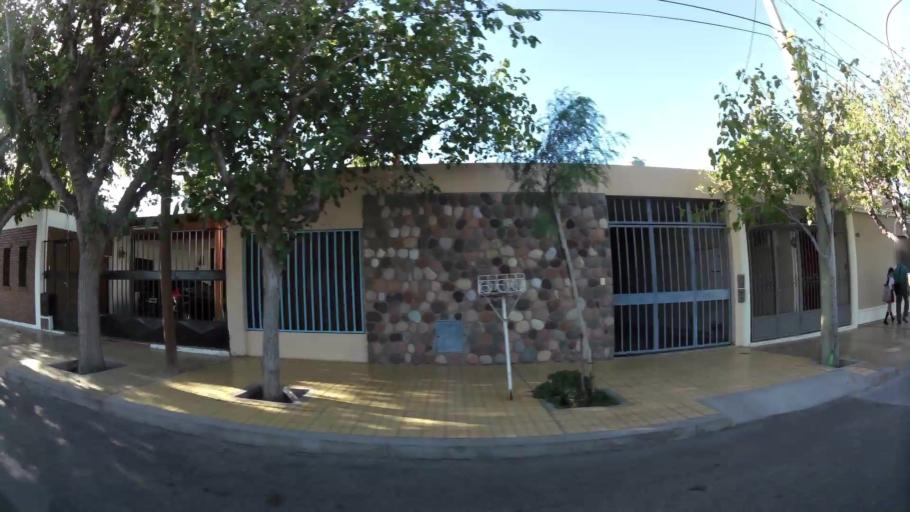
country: AR
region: San Juan
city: Villa Krause
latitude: -31.5508
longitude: -68.5187
